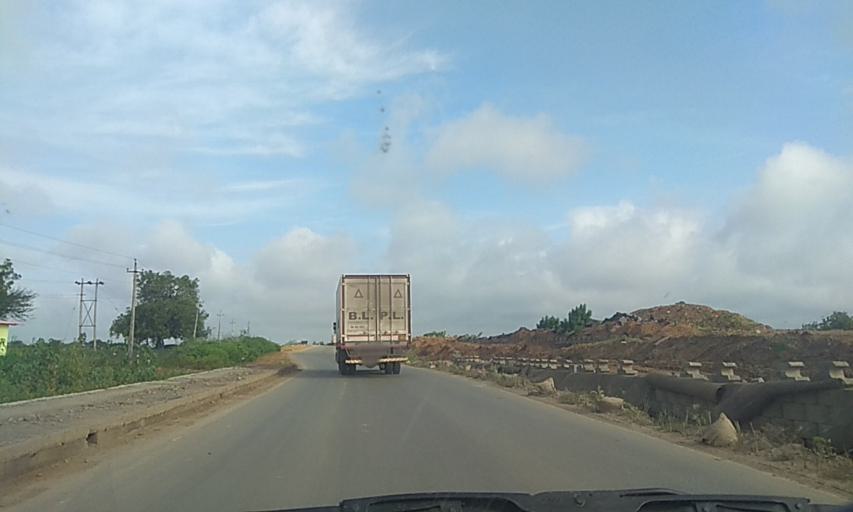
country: IN
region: Karnataka
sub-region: Haveri
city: Savanur
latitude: 14.8727
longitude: 75.3177
